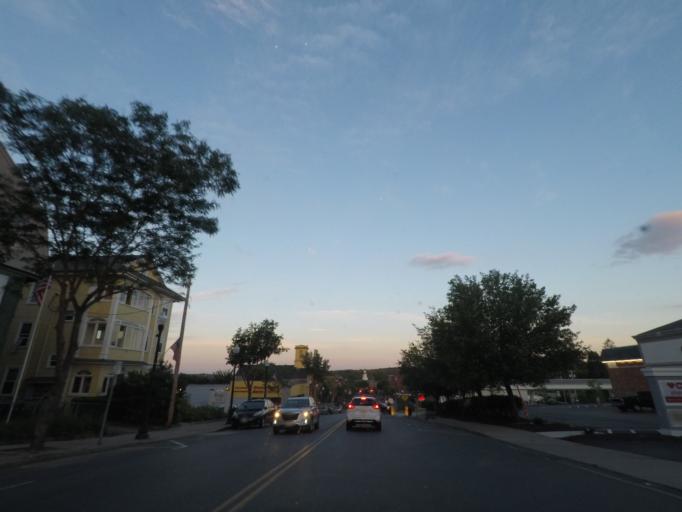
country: US
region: Massachusetts
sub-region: Worcester County
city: Southbridge
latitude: 42.0768
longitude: -72.0361
